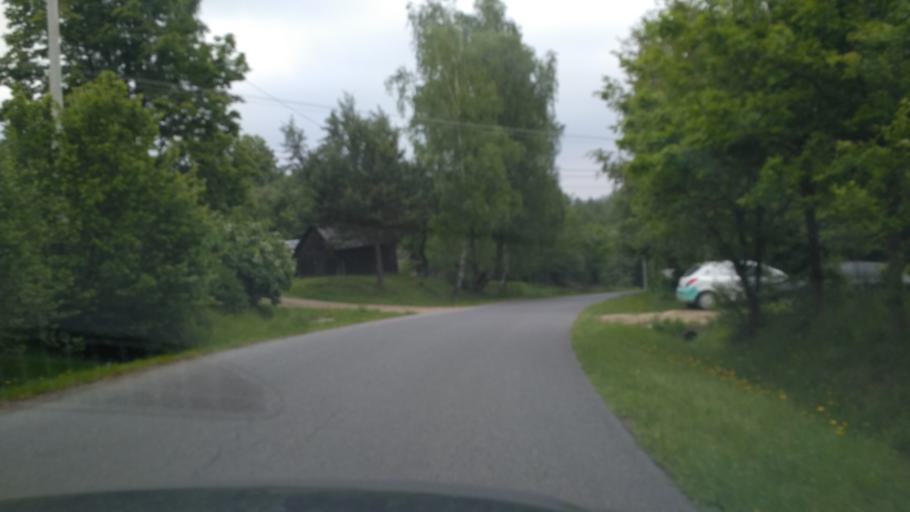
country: PL
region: Subcarpathian Voivodeship
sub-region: Powiat ropczycko-sedziszowski
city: Zagorzyce
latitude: 49.9933
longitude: 21.6939
